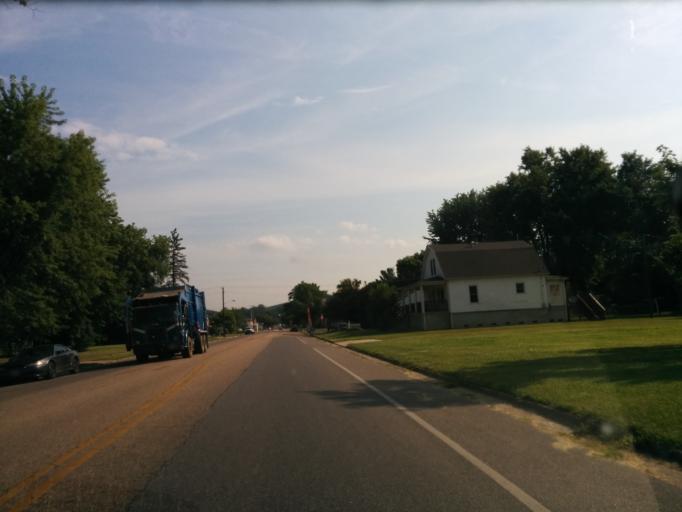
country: US
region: Virginia
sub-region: City of Buena Vista
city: Buena Vista
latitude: 37.7298
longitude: -79.3562
